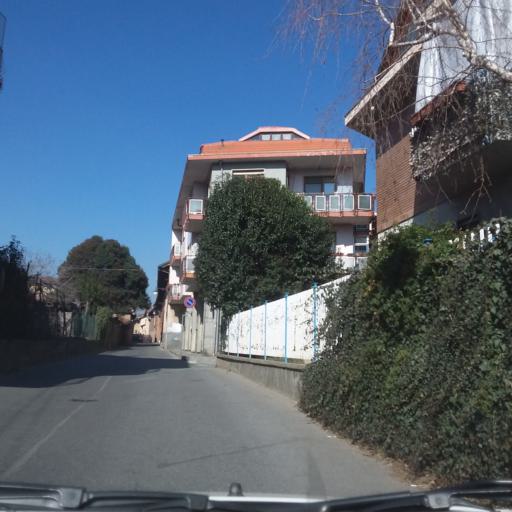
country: IT
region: Piedmont
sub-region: Provincia di Torino
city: Rivoli
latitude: 45.0645
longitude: 7.5166
